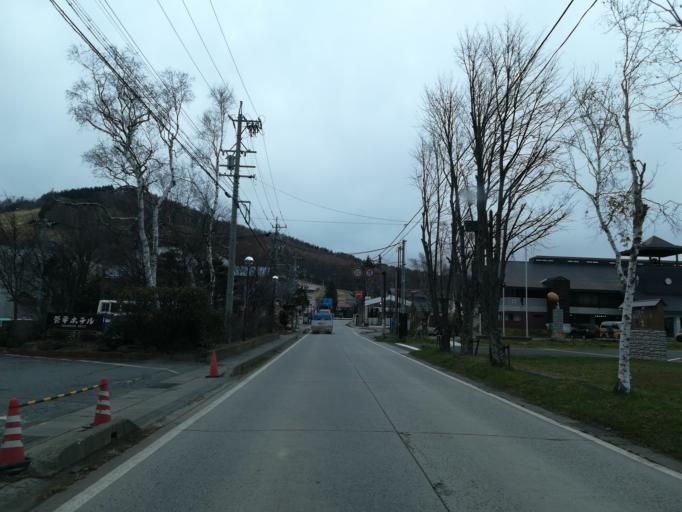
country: JP
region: Nagano
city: Suzaka
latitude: 36.5282
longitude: 138.3317
